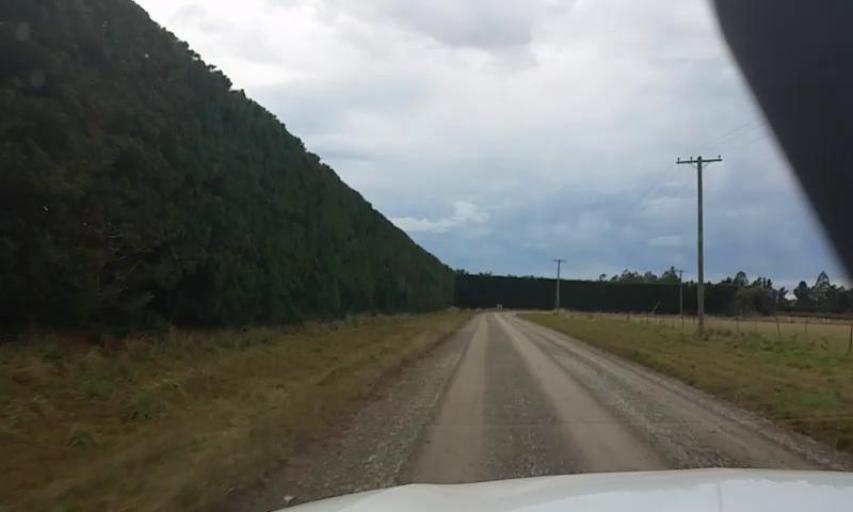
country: NZ
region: Canterbury
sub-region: Waimakariri District
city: Kaiapoi
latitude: -43.2908
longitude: 172.4448
